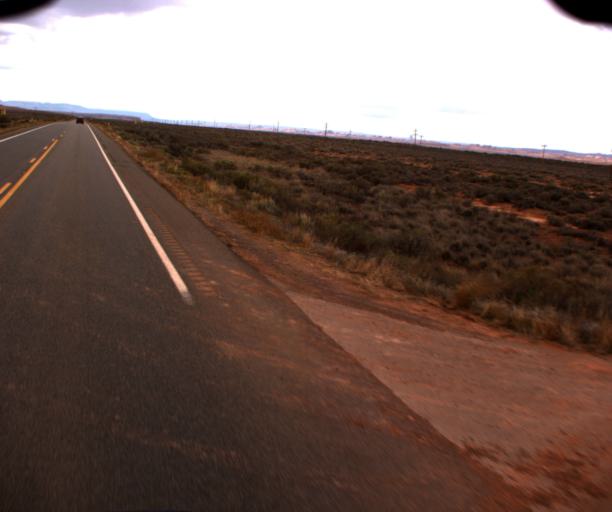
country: US
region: Arizona
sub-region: Navajo County
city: Kayenta
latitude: 36.8142
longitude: -109.8920
